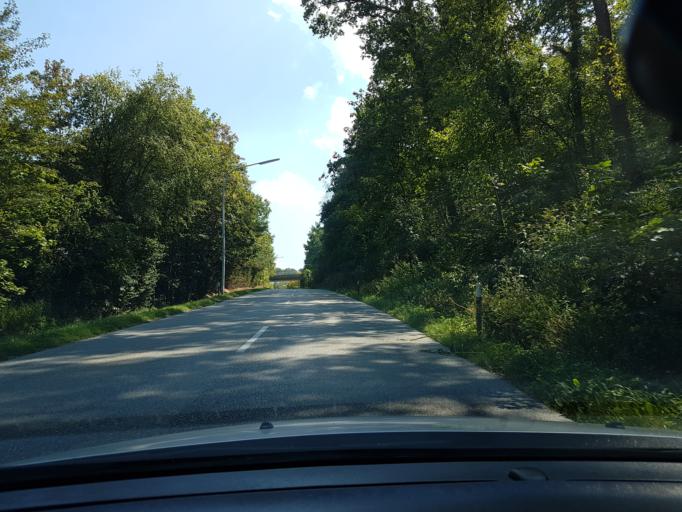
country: DE
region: Bavaria
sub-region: Upper Bavaria
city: Altoetting
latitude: 48.2407
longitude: 12.6726
